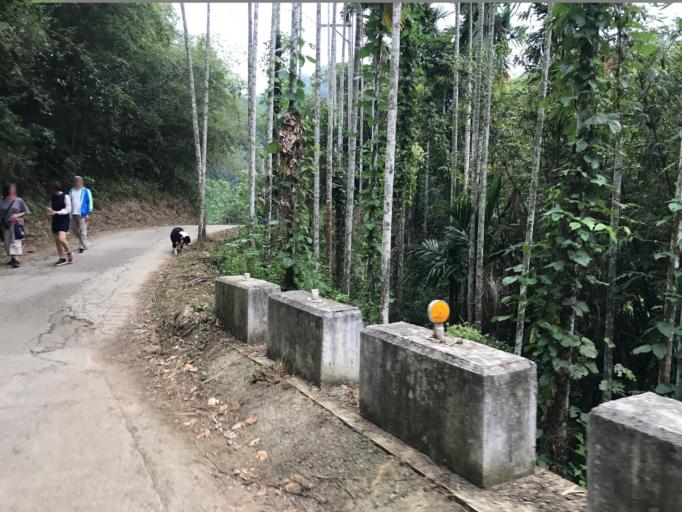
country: TW
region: Taiwan
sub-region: Miaoli
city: Miaoli
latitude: 24.6240
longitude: 120.9576
